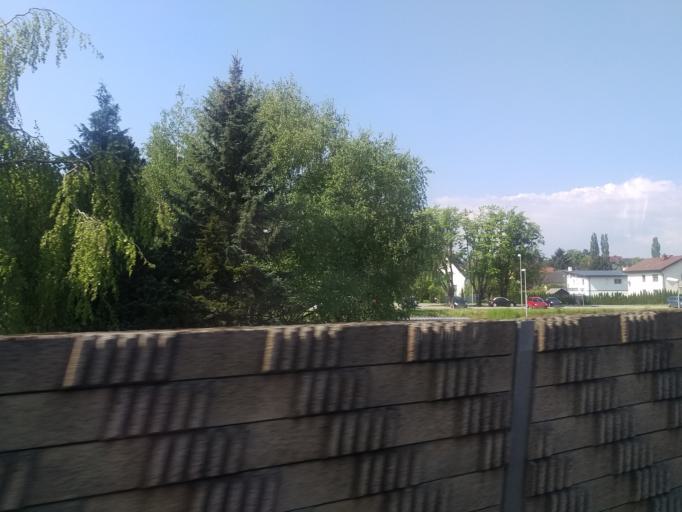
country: AT
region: Styria
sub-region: Politischer Bezirk Graz-Umgebung
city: Gratkorn
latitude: 47.1181
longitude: 15.3449
